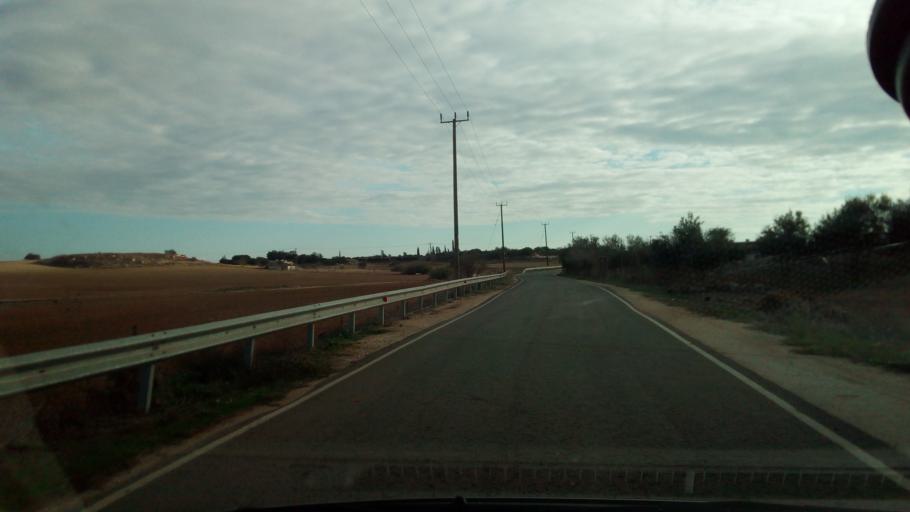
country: CY
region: Ammochostos
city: Frenaros
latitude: 35.0501
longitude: 33.8872
